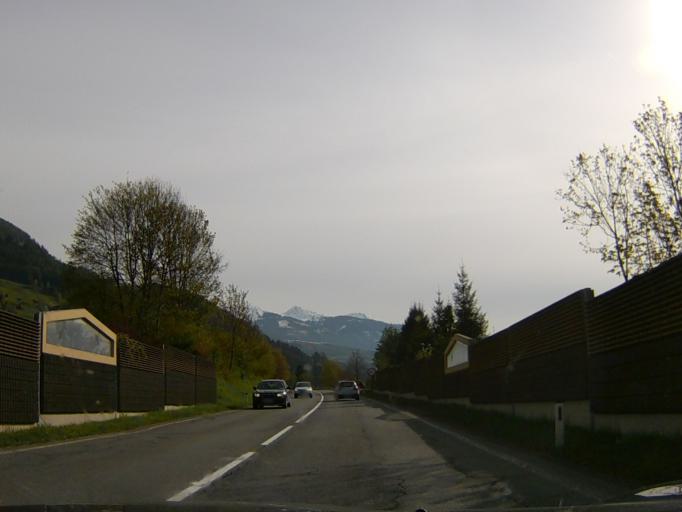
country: AT
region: Salzburg
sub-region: Politischer Bezirk Zell am See
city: Bramberg am Wildkogel
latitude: 47.2745
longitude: 12.3638
